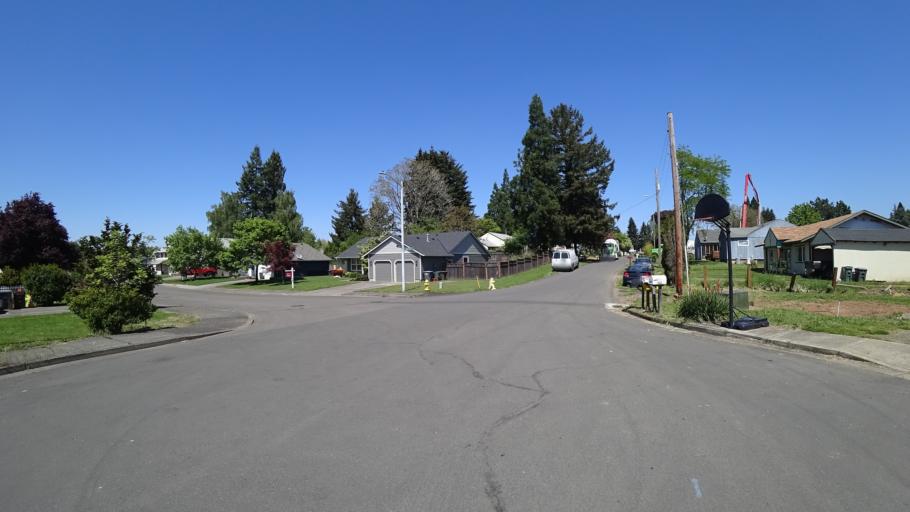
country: US
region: Oregon
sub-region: Washington County
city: Hillsboro
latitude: 45.5042
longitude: -122.9668
